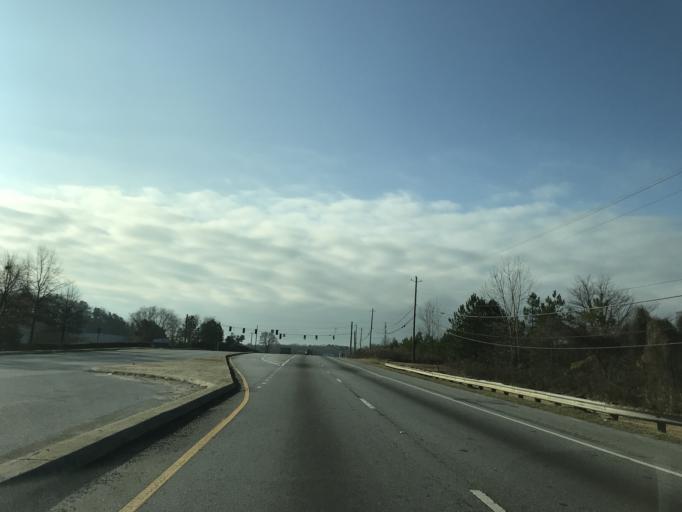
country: US
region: Georgia
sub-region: Clayton County
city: Forest Park
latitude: 33.6109
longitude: -84.4030
